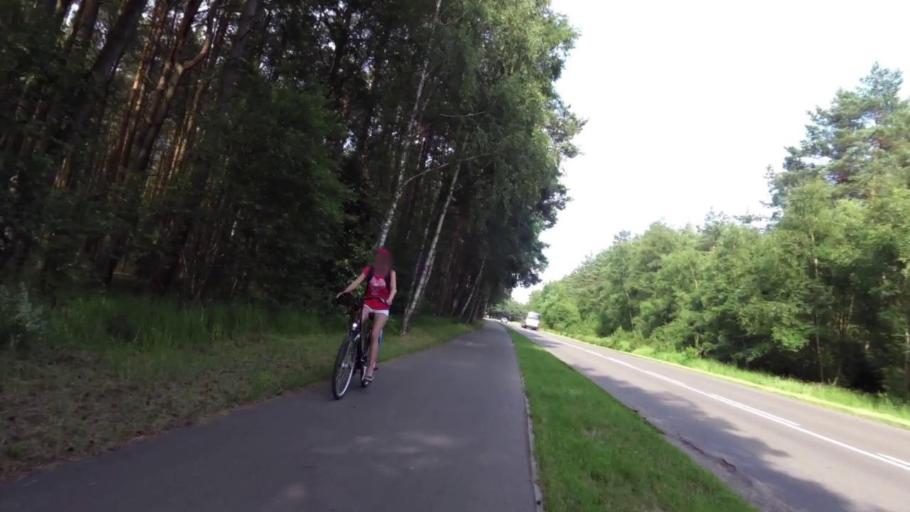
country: PL
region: West Pomeranian Voivodeship
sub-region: Powiat kolobrzeski
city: Grzybowo
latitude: 54.1620
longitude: 15.4484
